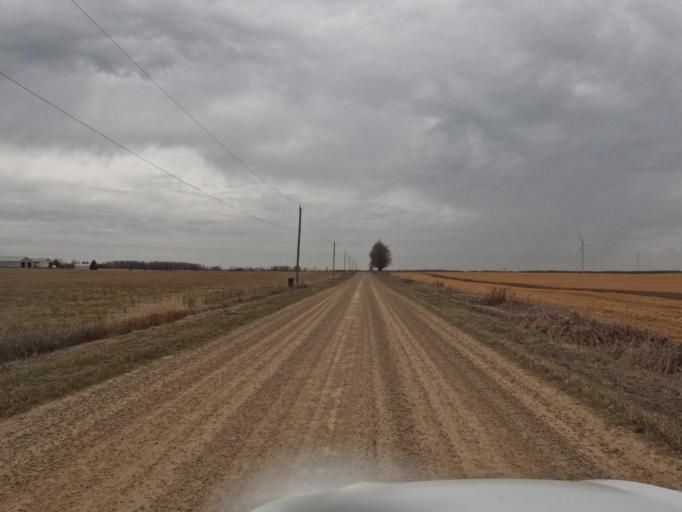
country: CA
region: Ontario
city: Shelburne
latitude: 43.8801
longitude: -80.3808
